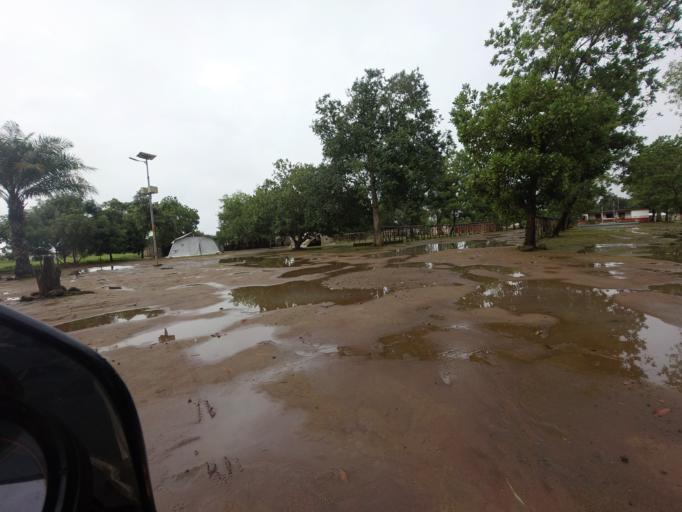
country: SL
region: Northern Province
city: Kambia
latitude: 9.1008
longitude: -12.9181
